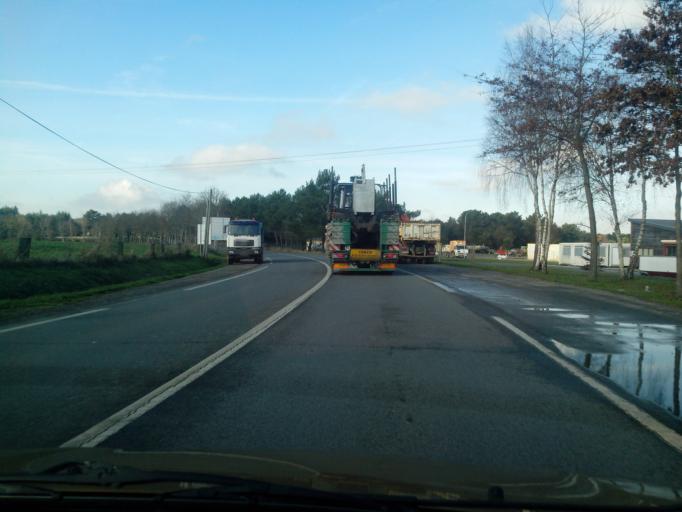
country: FR
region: Brittany
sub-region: Departement du Morbihan
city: Molac
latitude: 47.7789
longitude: -2.4553
